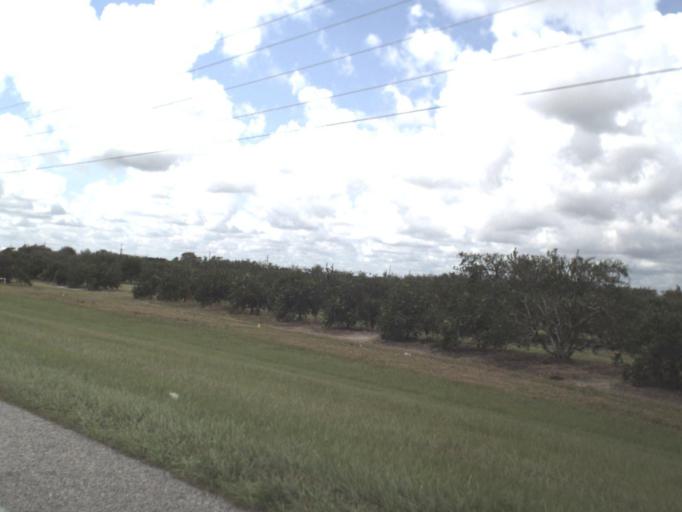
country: US
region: Florida
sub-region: Hardee County
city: Wauchula
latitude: 27.5190
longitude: -81.8092
